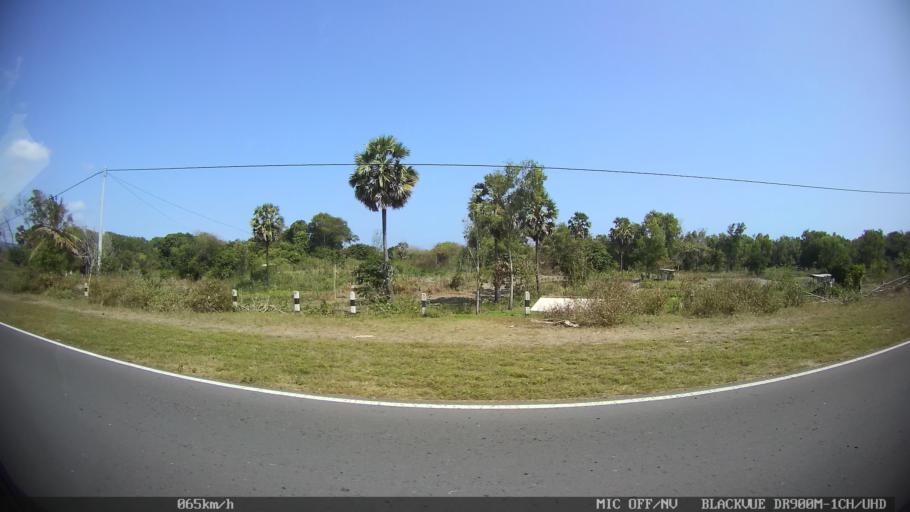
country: ID
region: Daerah Istimewa Yogyakarta
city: Bambanglipuro
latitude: -8.0110
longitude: 110.3066
